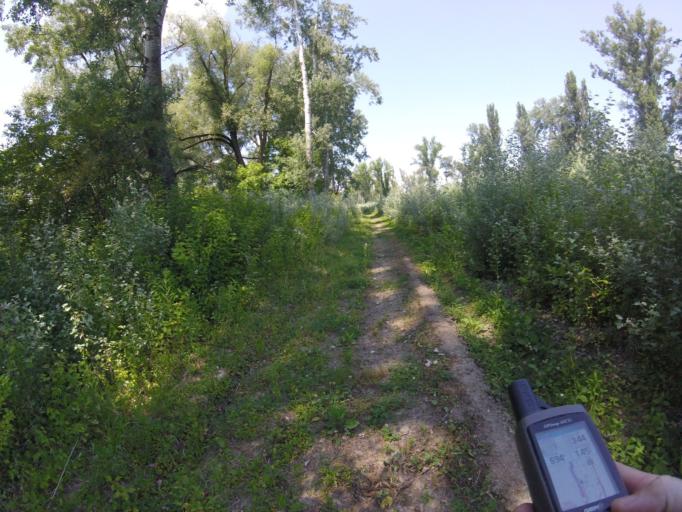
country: HR
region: Osjecko-Baranjska
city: Viljevo
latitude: 45.7826
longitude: 18.1009
